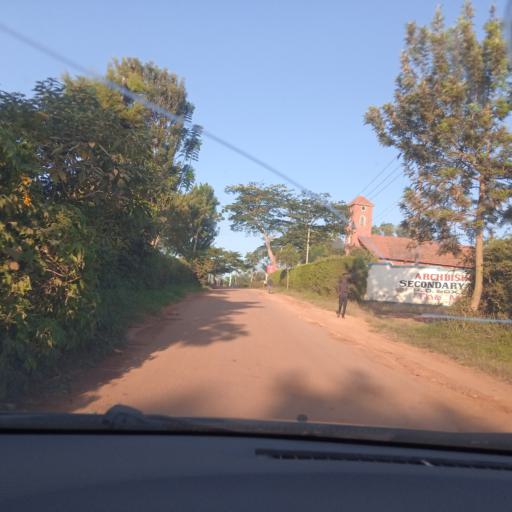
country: UG
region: Central Region
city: Masaka
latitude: -0.3309
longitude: 31.7596
